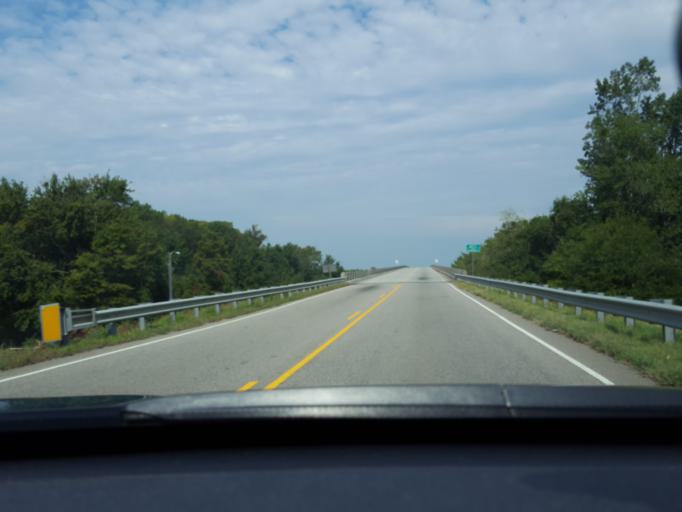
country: US
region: North Carolina
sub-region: Washington County
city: Plymouth
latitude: 35.9123
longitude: -76.7197
